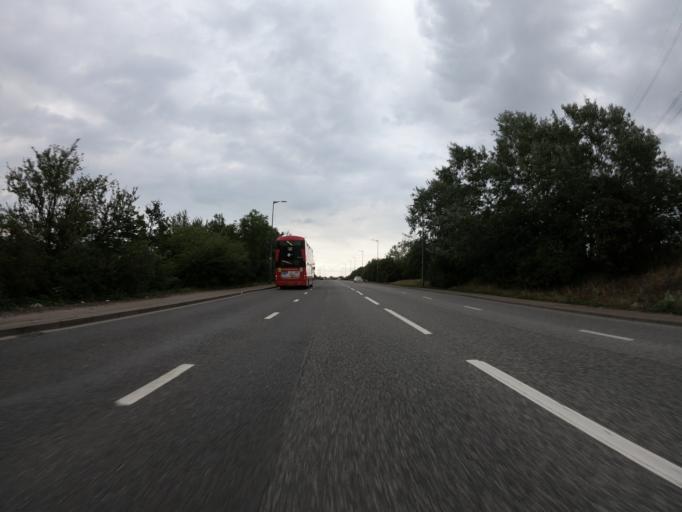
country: GB
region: England
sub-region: Greater London
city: Barking
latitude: 51.5171
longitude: 0.0726
